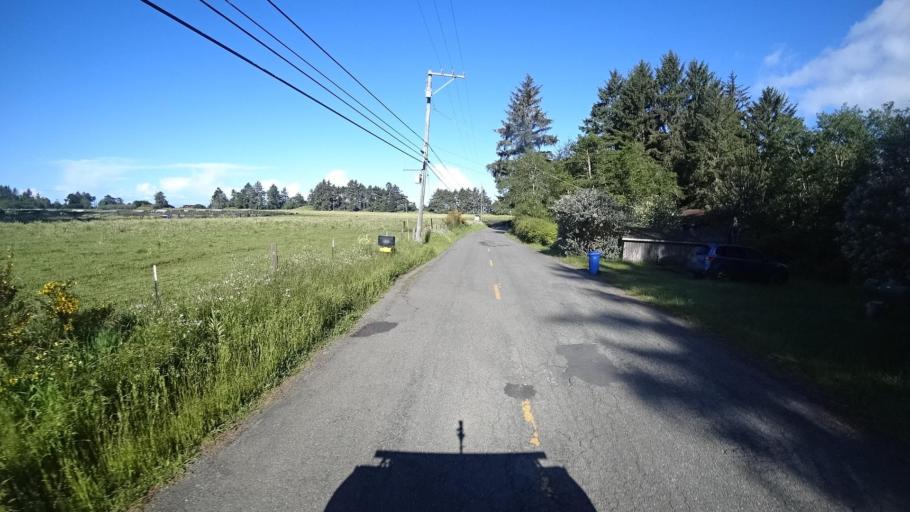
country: US
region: California
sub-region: Humboldt County
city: Westhaven-Moonstone
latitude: 41.0052
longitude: -124.1046
